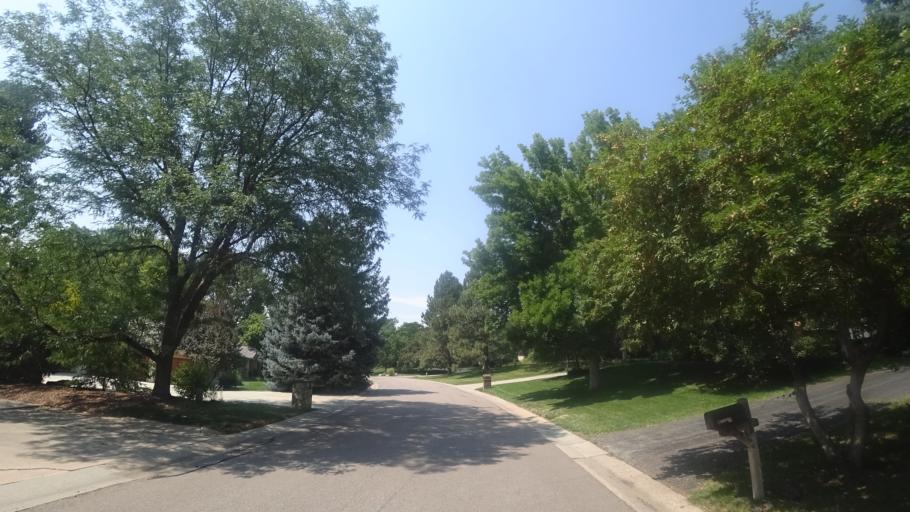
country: US
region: Colorado
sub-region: Arapahoe County
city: Greenwood Village
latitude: 39.6125
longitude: -104.9740
